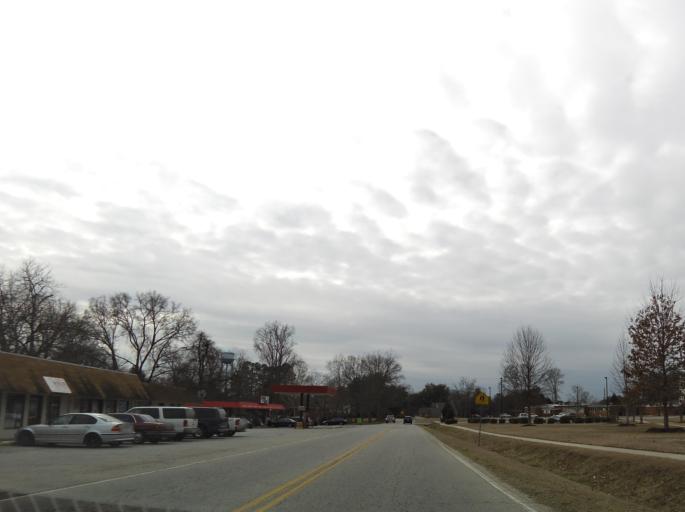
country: US
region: Georgia
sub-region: Peach County
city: Byron
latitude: 32.6541
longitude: -83.7604
